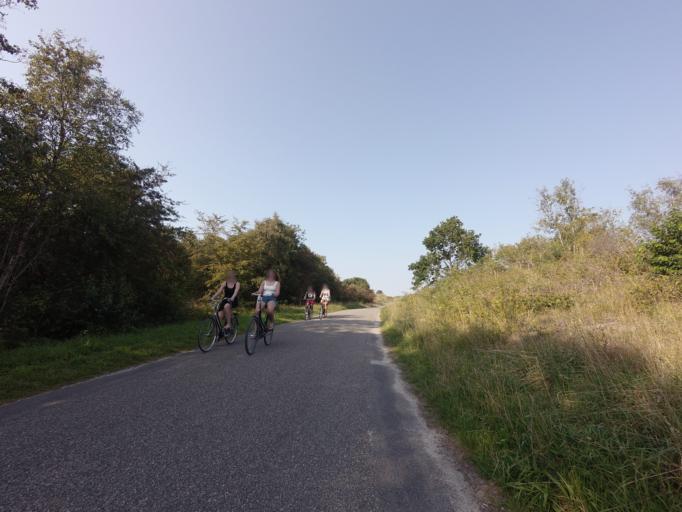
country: NL
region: Friesland
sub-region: Gemeente Schiermonnikoog
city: Schiermonnikoog
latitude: 53.4857
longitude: 6.1789
